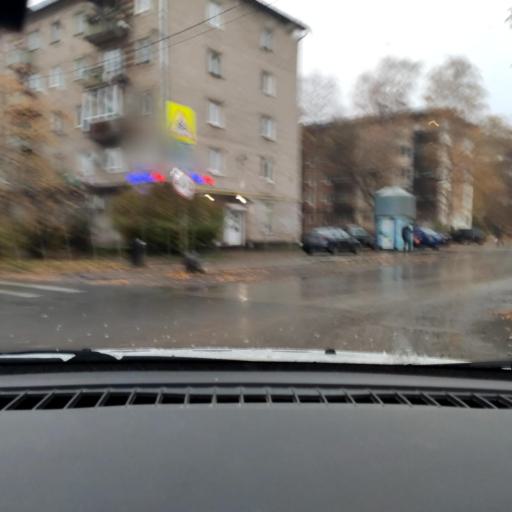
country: RU
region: Perm
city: Kondratovo
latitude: 58.0488
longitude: 56.0948
